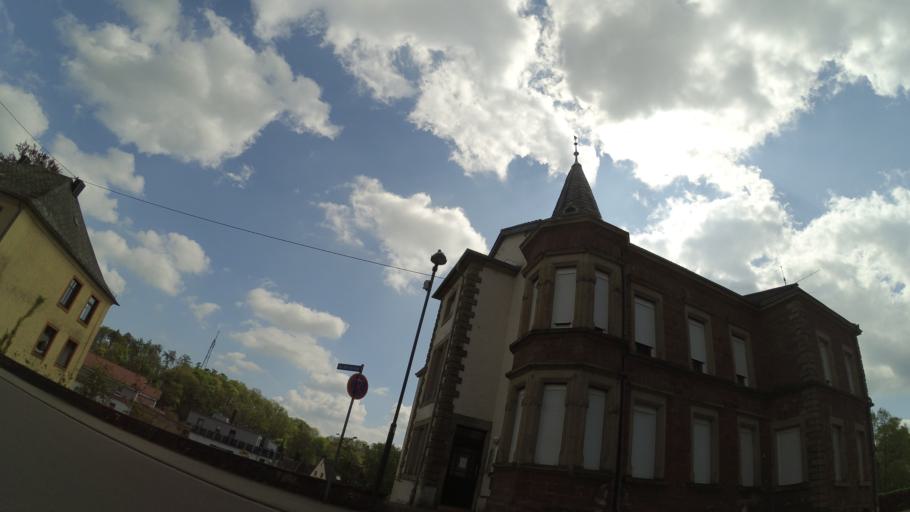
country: DE
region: Saarland
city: Wadern
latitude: 49.5381
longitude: 6.8896
